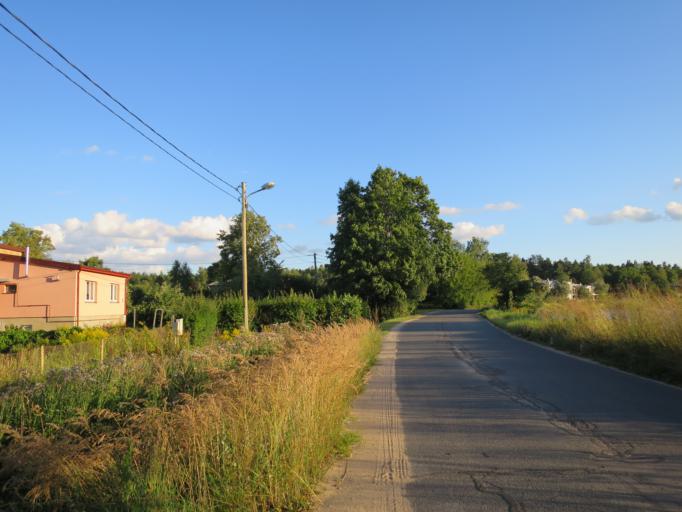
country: LV
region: Riga
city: Bergi
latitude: 57.0057
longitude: 24.2707
